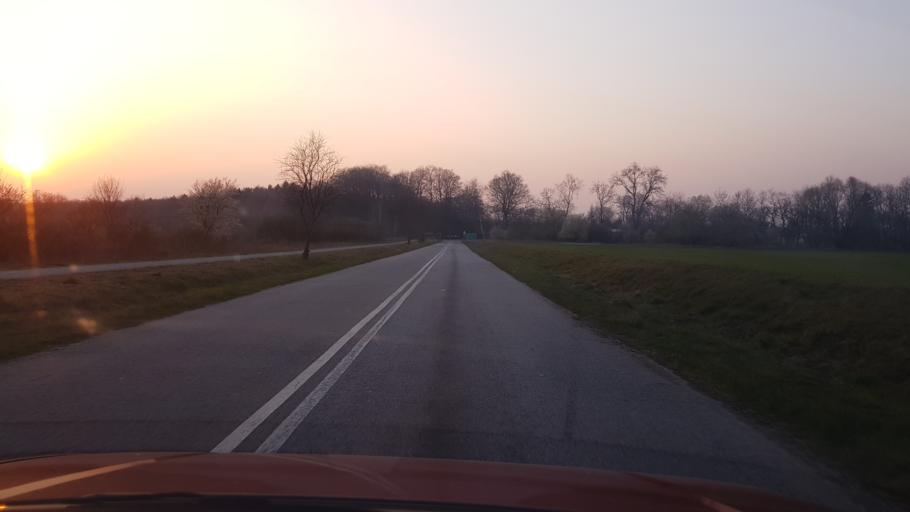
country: PL
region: West Pomeranian Voivodeship
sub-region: Powiat lobeski
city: Radowo Male
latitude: 53.6817
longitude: 15.4251
